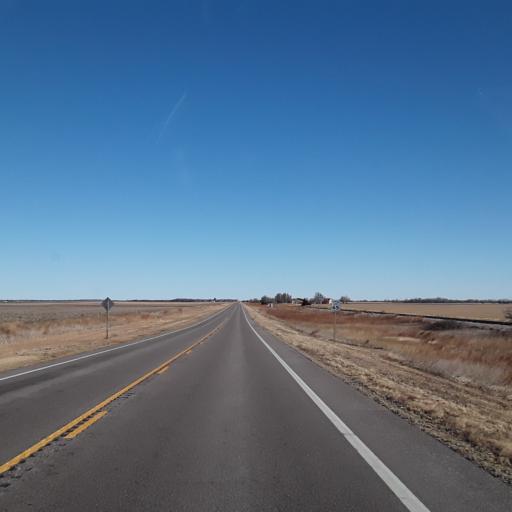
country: US
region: Kansas
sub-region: Pawnee County
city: Larned
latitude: 38.0904
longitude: -99.2219
